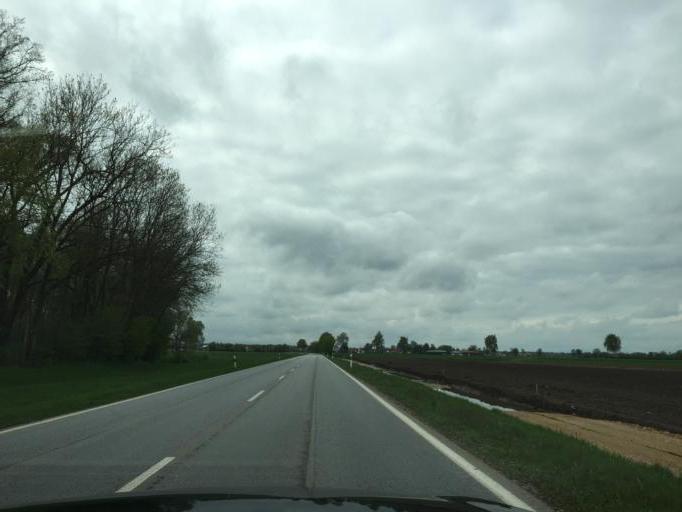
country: DE
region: Bavaria
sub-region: Swabia
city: Binswangen
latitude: 48.5713
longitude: 10.6125
